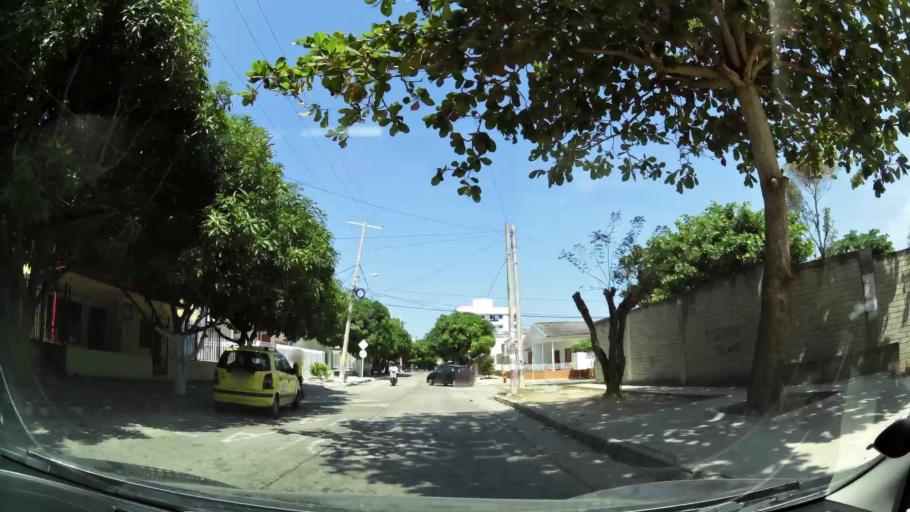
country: CO
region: Atlantico
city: Barranquilla
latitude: 10.9674
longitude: -74.8024
